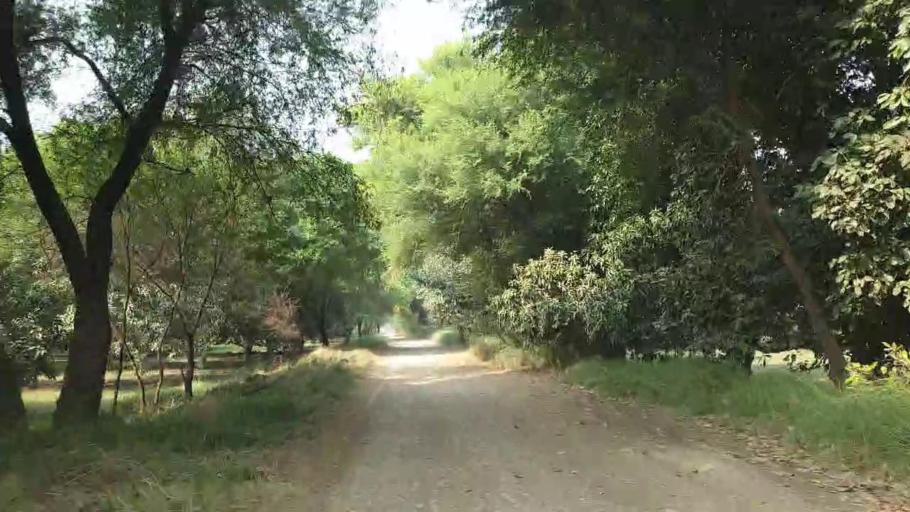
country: PK
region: Sindh
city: Tando Muhammad Khan
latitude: 25.2107
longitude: 68.5586
